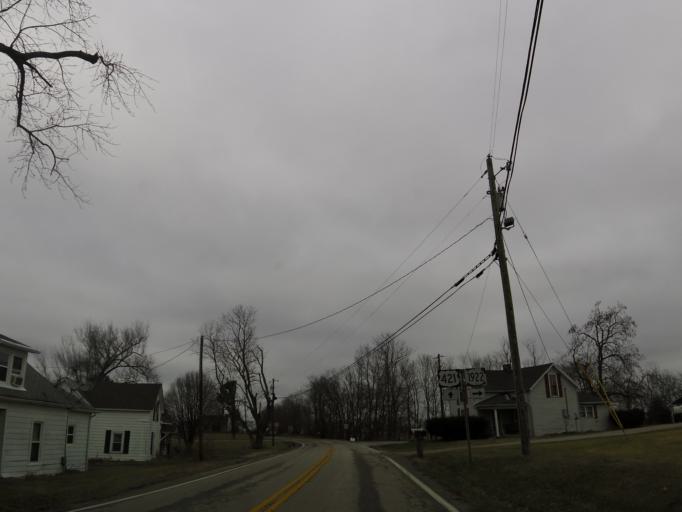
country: US
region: Kentucky
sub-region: Henry County
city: Eminence
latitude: 38.3416
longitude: -85.0517
